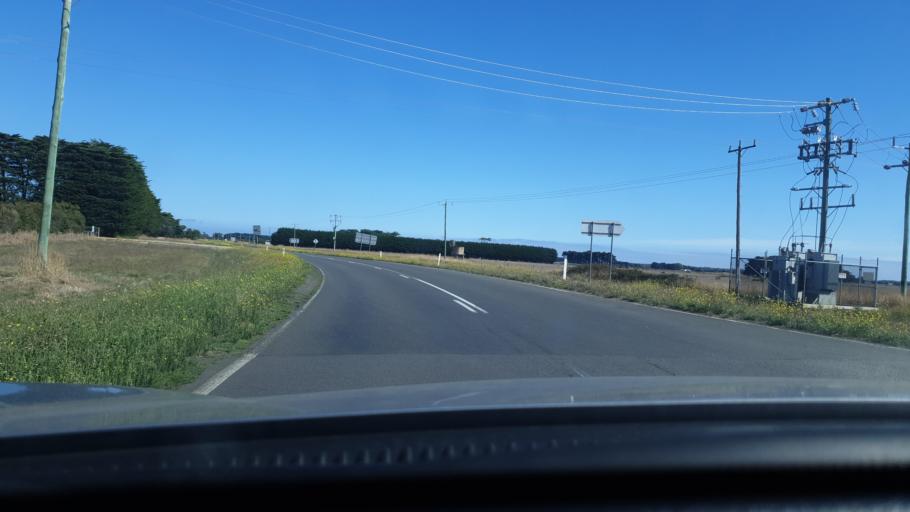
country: AU
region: Victoria
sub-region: Moyne
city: Port Fairy
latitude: -38.2856
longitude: 142.3106
